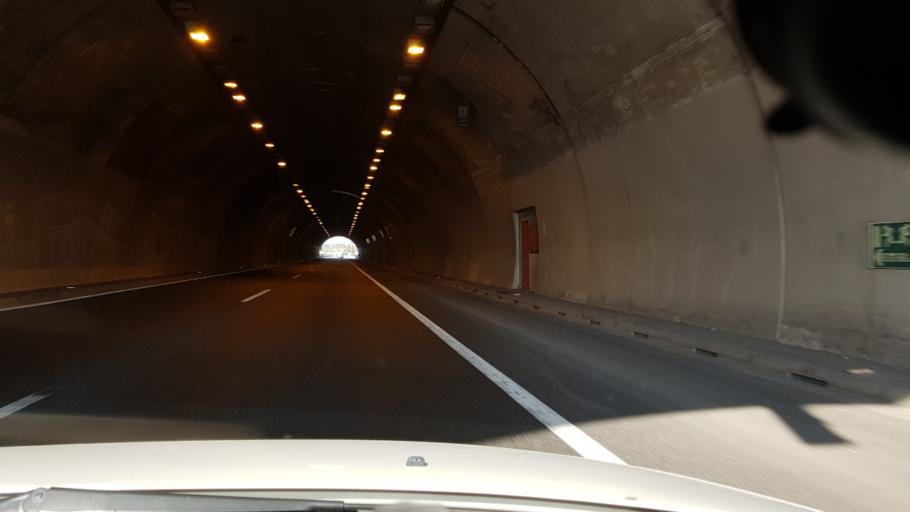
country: SI
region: Trzic
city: Bistrica pri Trzicu
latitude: 46.3177
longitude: 14.2462
